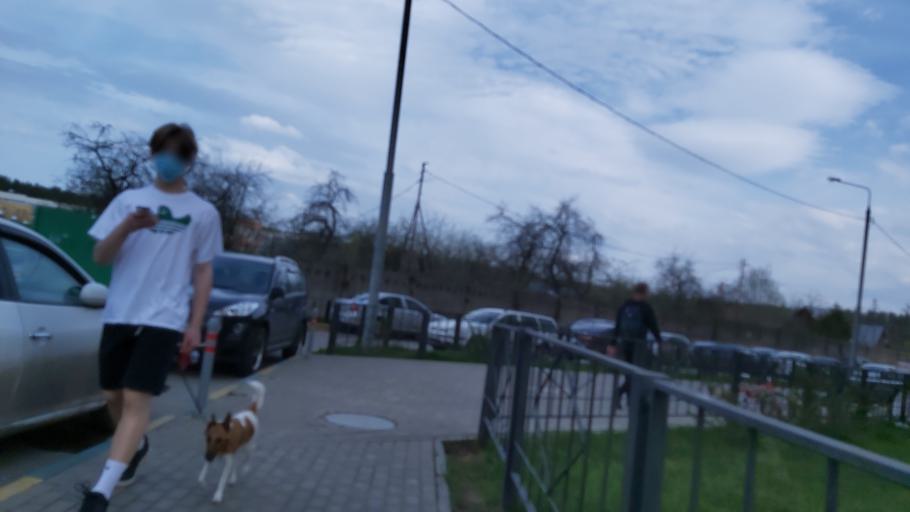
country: RU
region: Moskovskaya
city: Korolev
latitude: 55.9110
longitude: 37.8301
